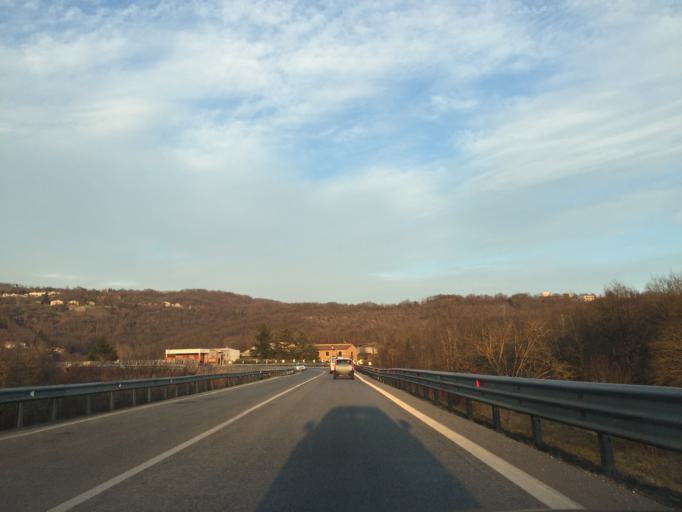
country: IT
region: Molise
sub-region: Provincia di Campobasso
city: Vinchiaturo
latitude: 41.4937
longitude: 14.6075
